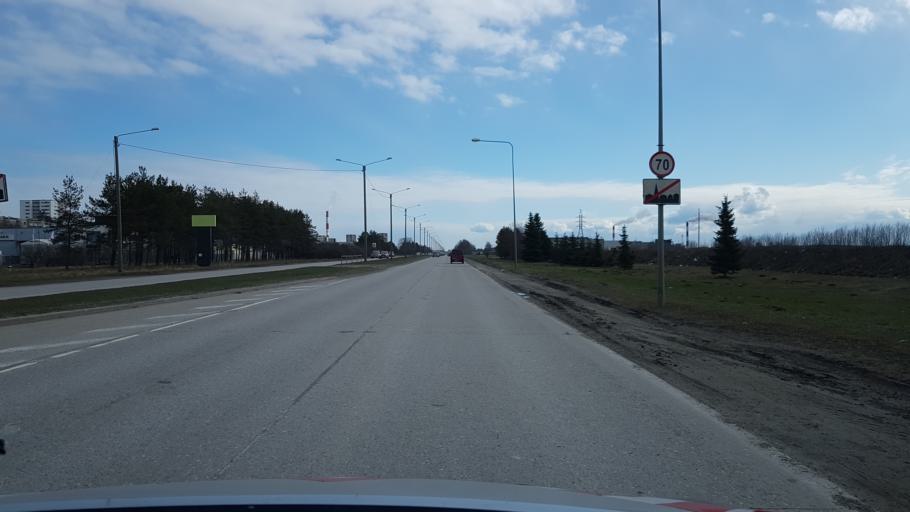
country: EE
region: Harju
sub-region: Tallinna linn
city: Kose
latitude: 59.4365
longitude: 24.8755
